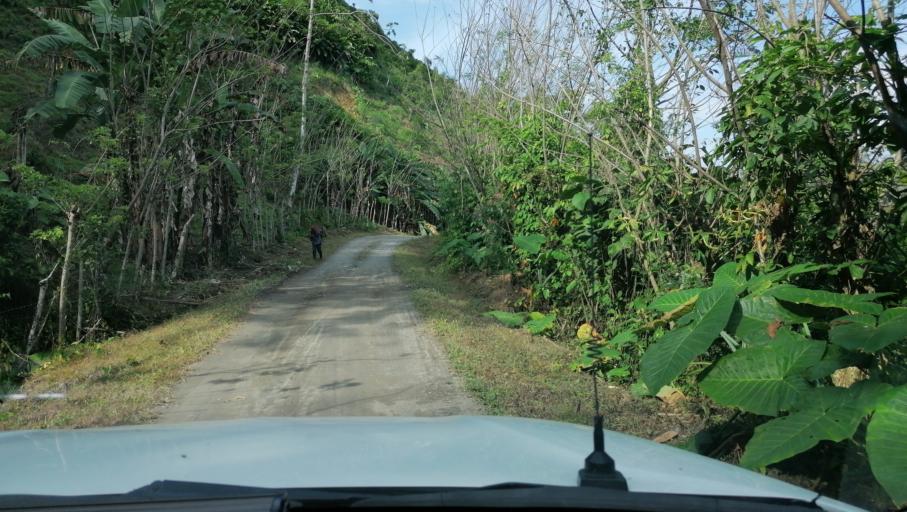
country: MX
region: Chiapas
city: Ostuacan
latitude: 17.4530
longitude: -93.2448
